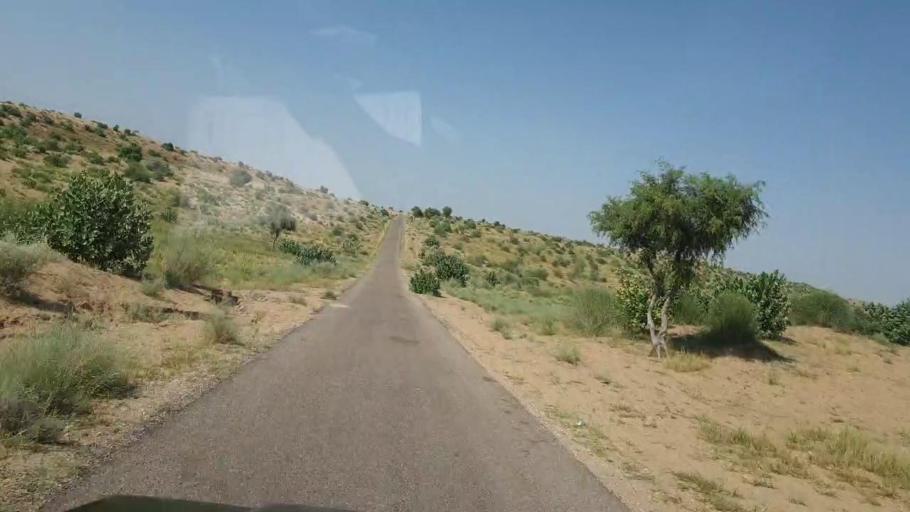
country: PK
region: Sindh
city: Chor
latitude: 25.6224
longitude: 70.3173
